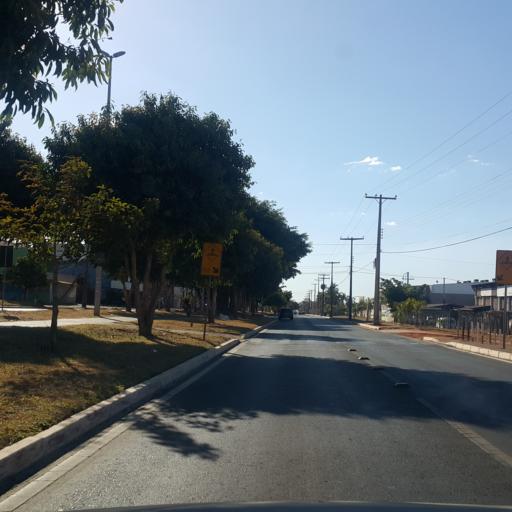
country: BR
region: Federal District
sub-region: Brasilia
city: Brasilia
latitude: -15.8107
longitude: -48.1000
